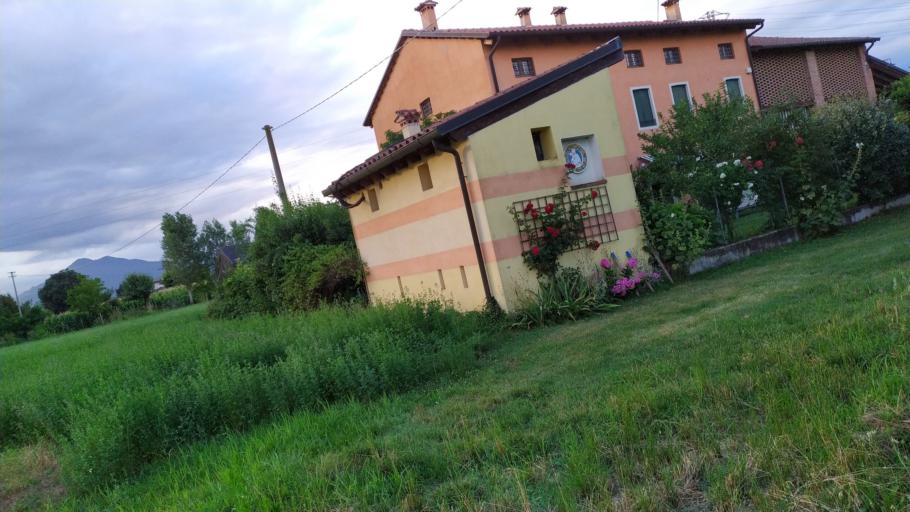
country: IT
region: Veneto
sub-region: Provincia di Vicenza
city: Villaverla
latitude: 45.6522
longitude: 11.4662
